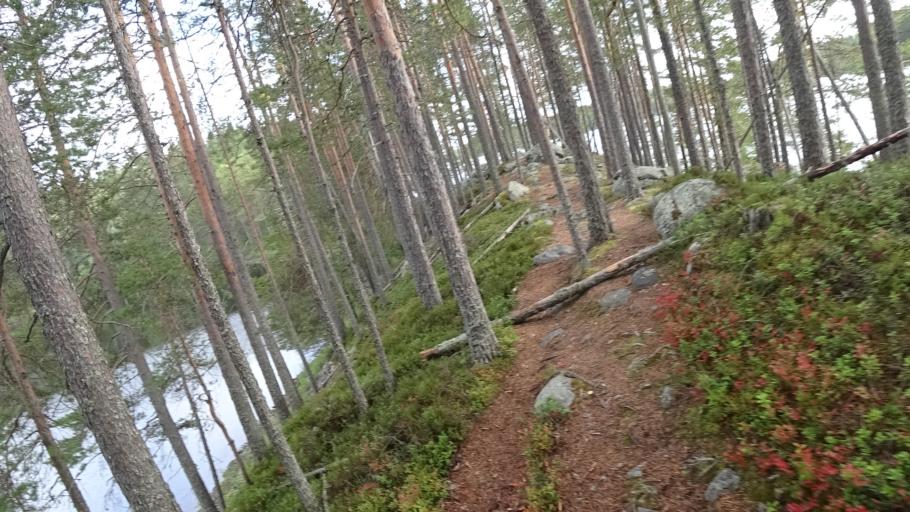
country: FI
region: North Karelia
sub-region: Joensuu
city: Ilomantsi
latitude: 62.5738
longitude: 31.1727
